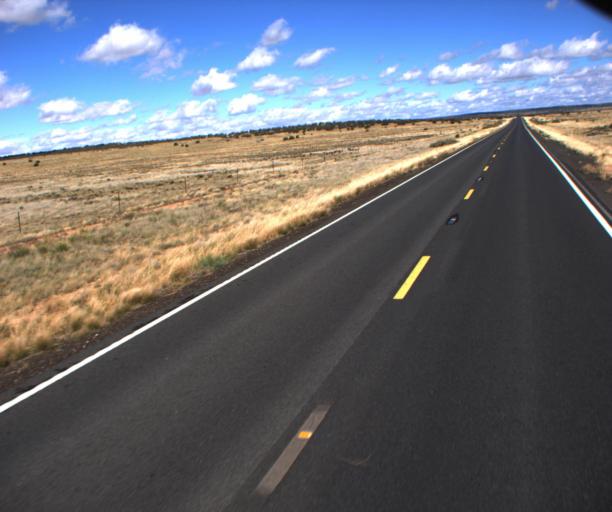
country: US
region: Arizona
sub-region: Apache County
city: Houck
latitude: 34.9833
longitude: -109.2270
